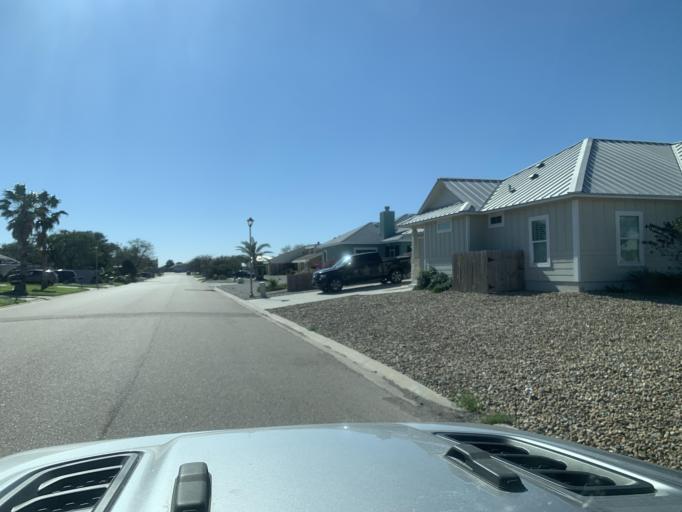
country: US
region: Texas
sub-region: Nueces County
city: Corpus Christi
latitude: 27.6273
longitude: -97.2269
